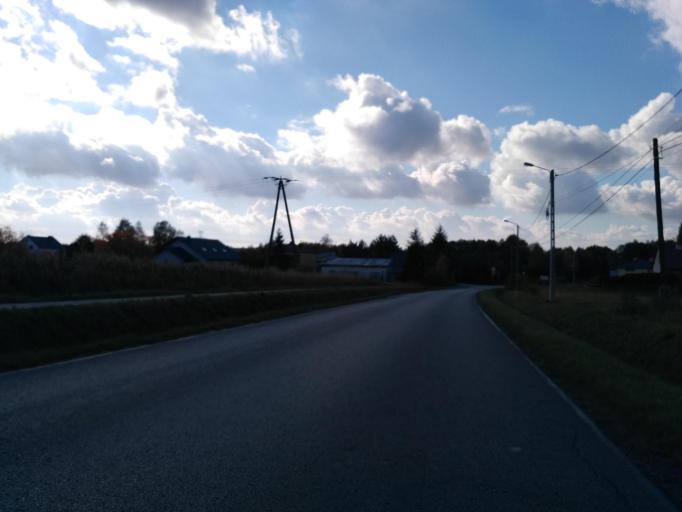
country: PL
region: Subcarpathian Voivodeship
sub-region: Powiat rzeszowski
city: Glogow Malopolski
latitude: 50.1450
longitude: 21.9494
